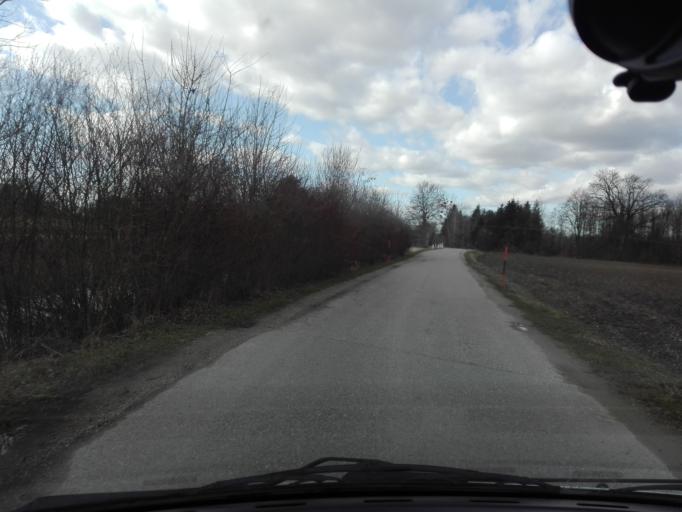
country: AT
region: Upper Austria
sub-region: Politischer Bezirk Perg
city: Perg
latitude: 48.2249
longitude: 14.6589
